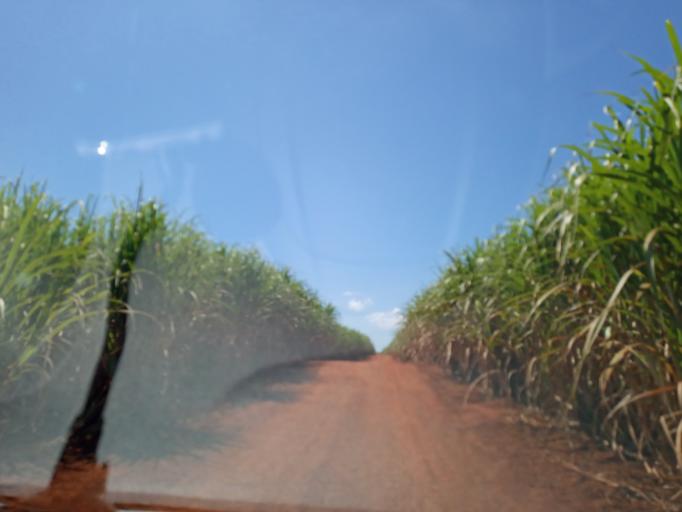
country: BR
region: Goias
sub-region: Itumbiara
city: Itumbiara
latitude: -18.4409
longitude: -49.1400
